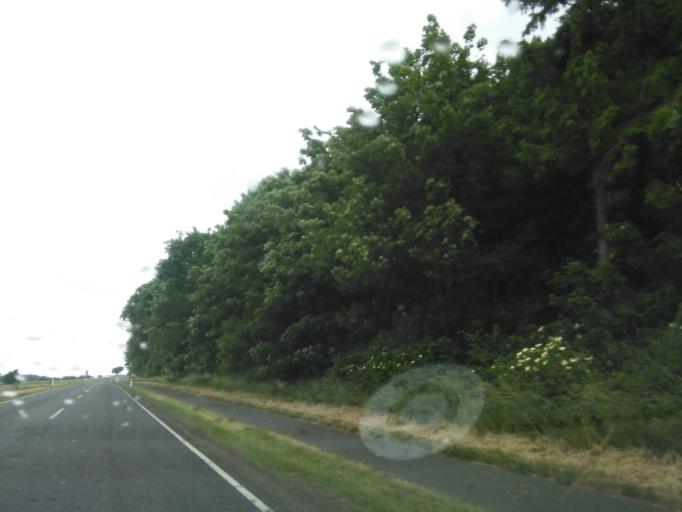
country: DK
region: Capital Region
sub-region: Bornholm Kommune
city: Akirkeby
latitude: 55.0471
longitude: 14.8328
